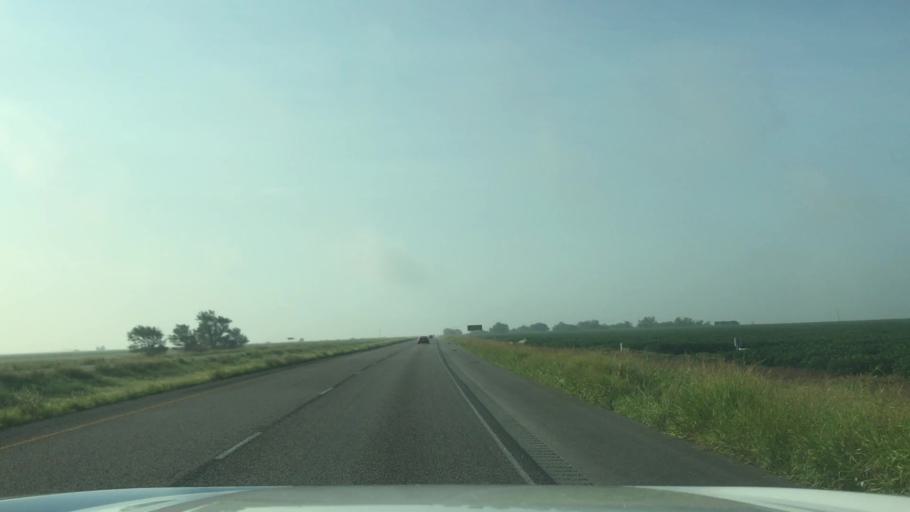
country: US
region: Texas
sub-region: Lubbock County
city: Slaton
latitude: 33.3521
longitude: -101.5506
